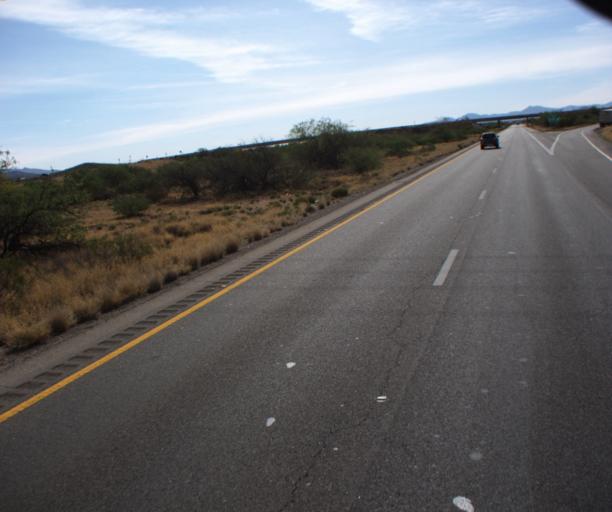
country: US
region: Arizona
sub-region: Pima County
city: Vail
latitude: 32.0293
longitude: -110.7240
